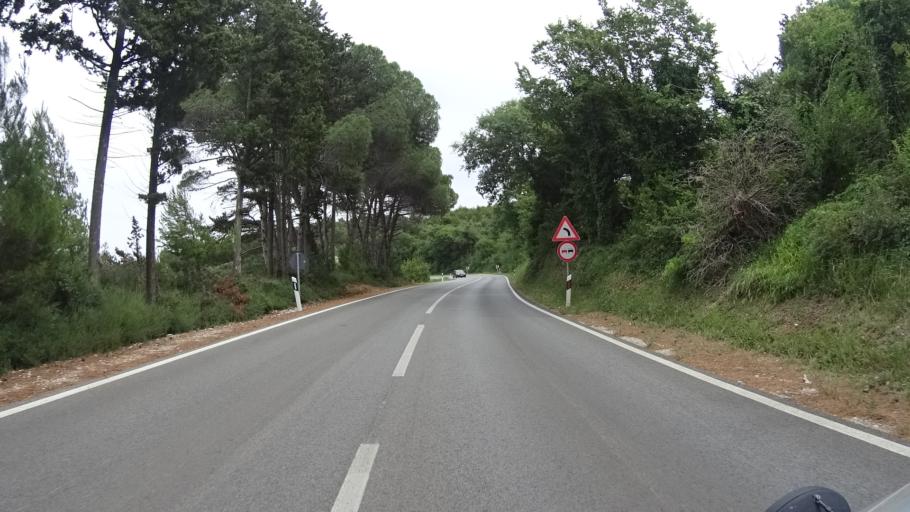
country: HR
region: Istarska
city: Medulin
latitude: 44.8163
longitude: 13.8908
